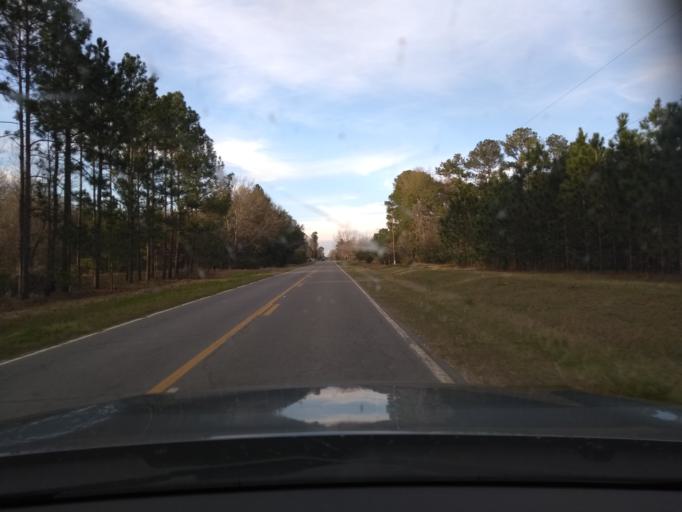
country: US
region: Georgia
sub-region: Bulloch County
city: Brooklet
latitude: 32.2580
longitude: -81.7624
